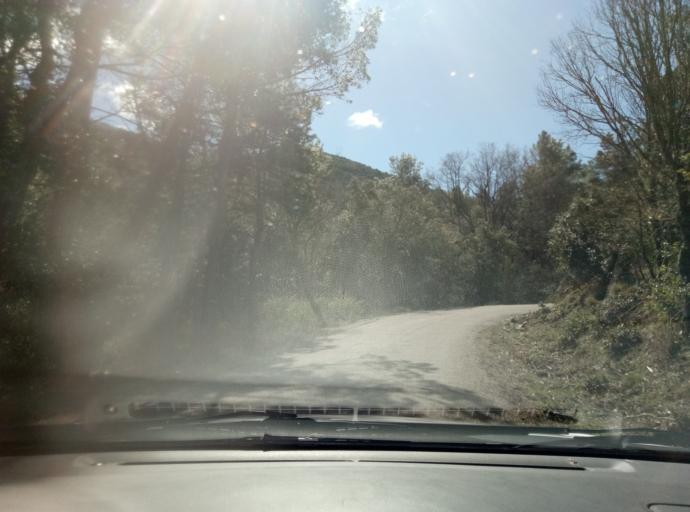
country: ES
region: Catalonia
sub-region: Provincia de Tarragona
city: Capafonts
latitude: 41.3459
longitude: 1.0586
